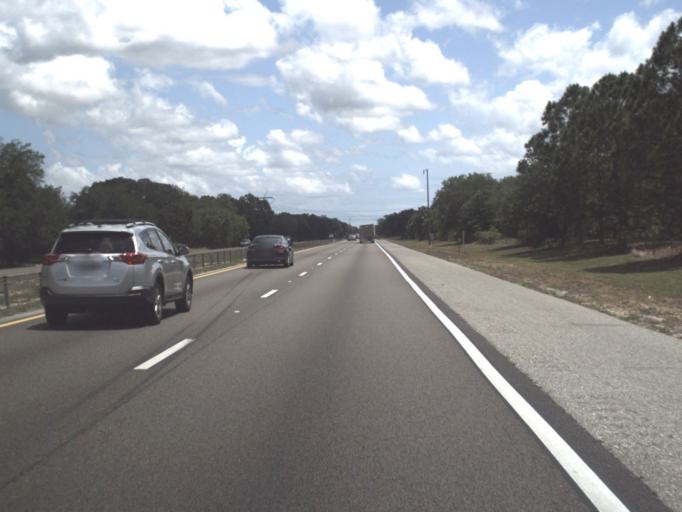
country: US
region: Florida
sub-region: Orange County
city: Wedgefield
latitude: 28.4523
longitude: -81.0189
